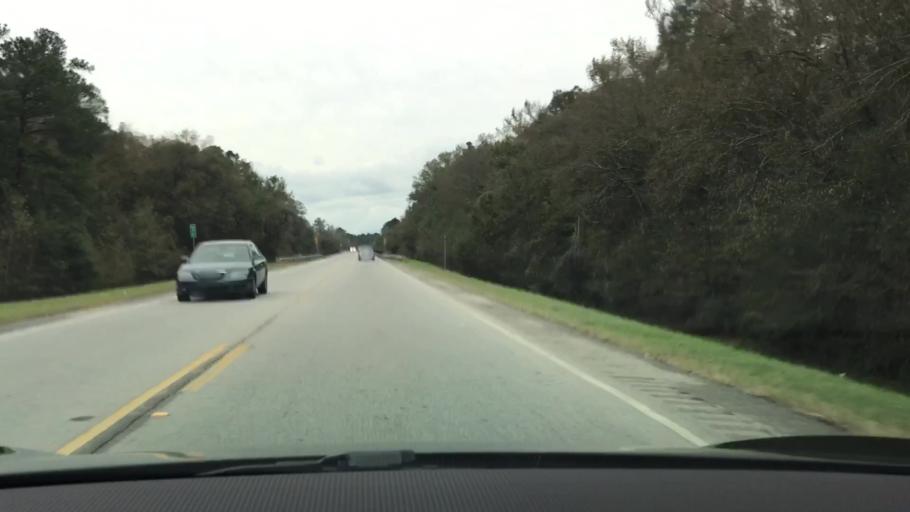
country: US
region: Georgia
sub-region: Jefferson County
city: Louisville
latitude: 32.9725
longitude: -82.3905
